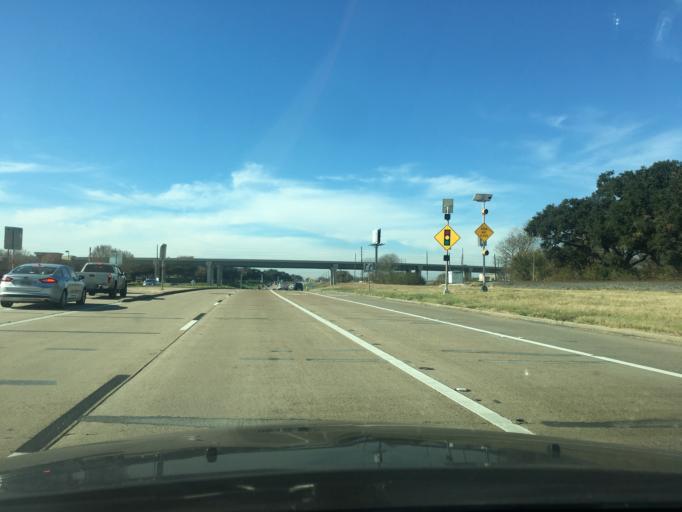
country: US
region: Texas
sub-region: Fort Bend County
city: New Territory
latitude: 29.6021
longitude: -95.6811
